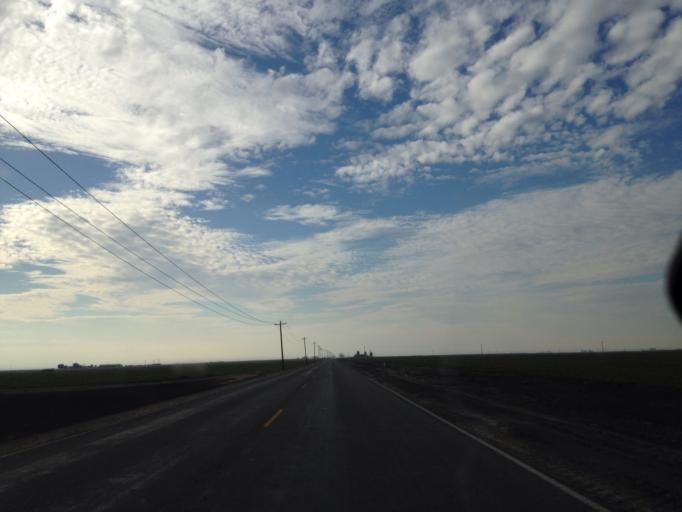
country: US
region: California
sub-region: Kern County
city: Buttonwillow
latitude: 35.4423
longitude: -119.5045
